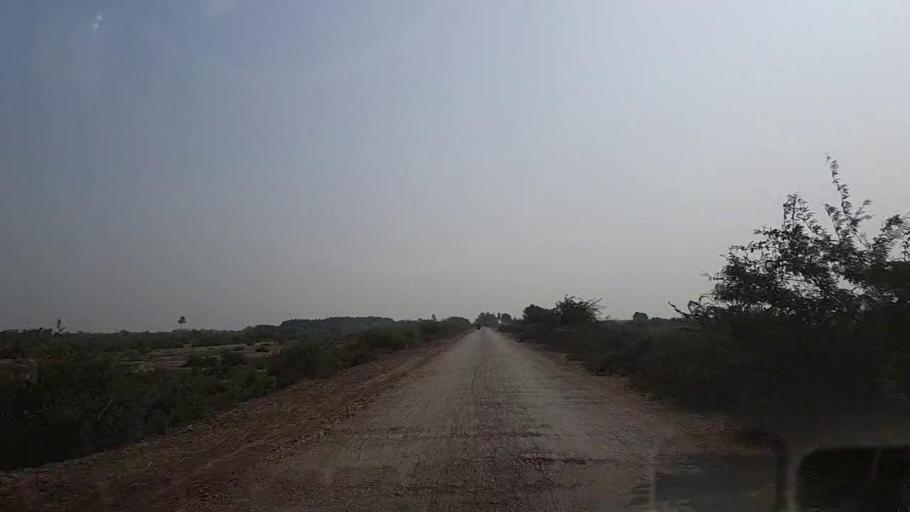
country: PK
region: Sindh
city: Keti Bandar
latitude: 24.2414
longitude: 67.6376
